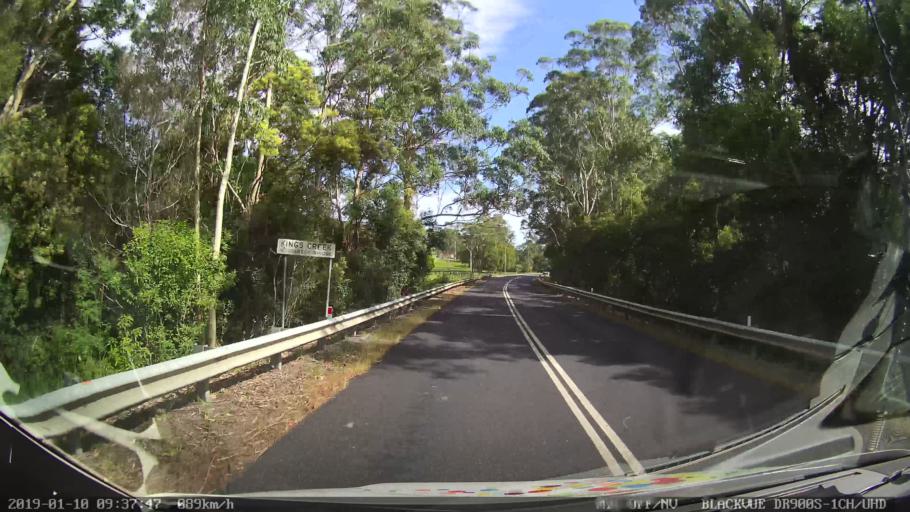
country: AU
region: New South Wales
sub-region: Coffs Harbour
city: Nana Glen
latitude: -30.1841
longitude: 153.0068
